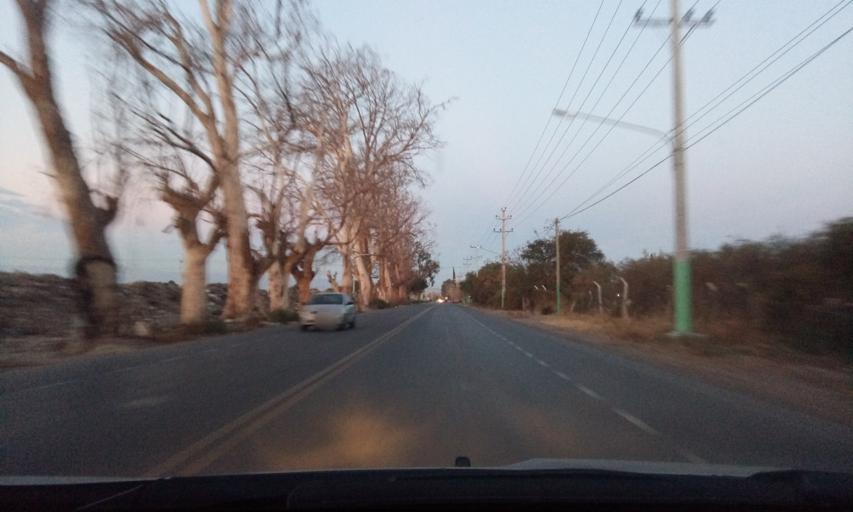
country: AR
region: San Juan
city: San Juan
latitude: -31.5496
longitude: -68.5732
